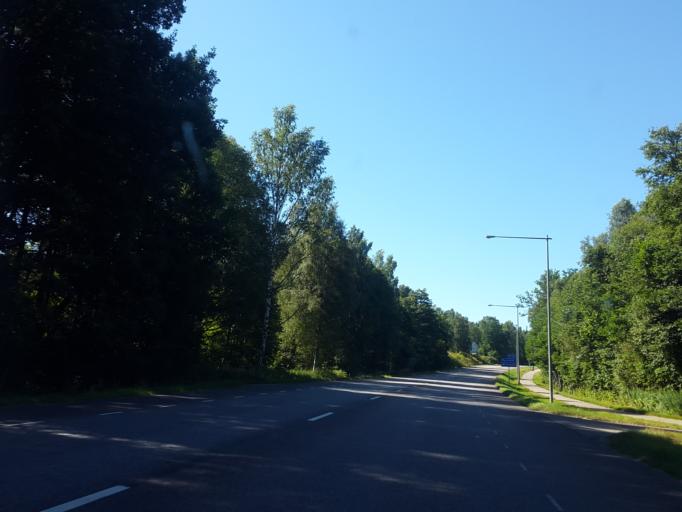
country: SE
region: Vaestra Goetaland
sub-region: Boras Kommun
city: Ganghester
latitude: 57.7963
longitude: 13.0099
